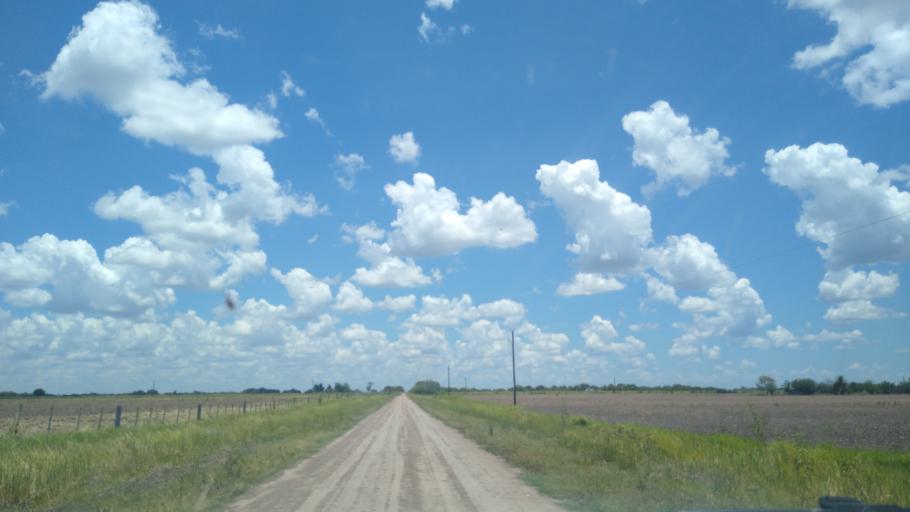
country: AR
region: Chaco
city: Presidencia Roque Saenz Pena
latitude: -26.7339
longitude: -60.3775
